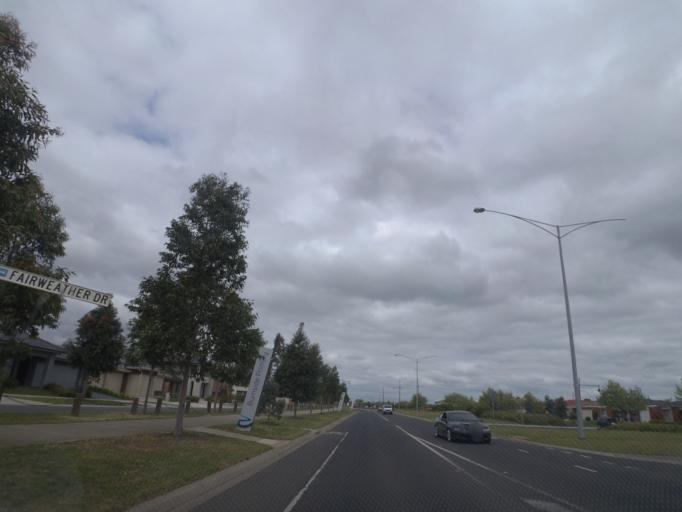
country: AU
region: Victoria
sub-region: Melton
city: Caroline Springs
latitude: -37.7454
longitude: 144.7492
